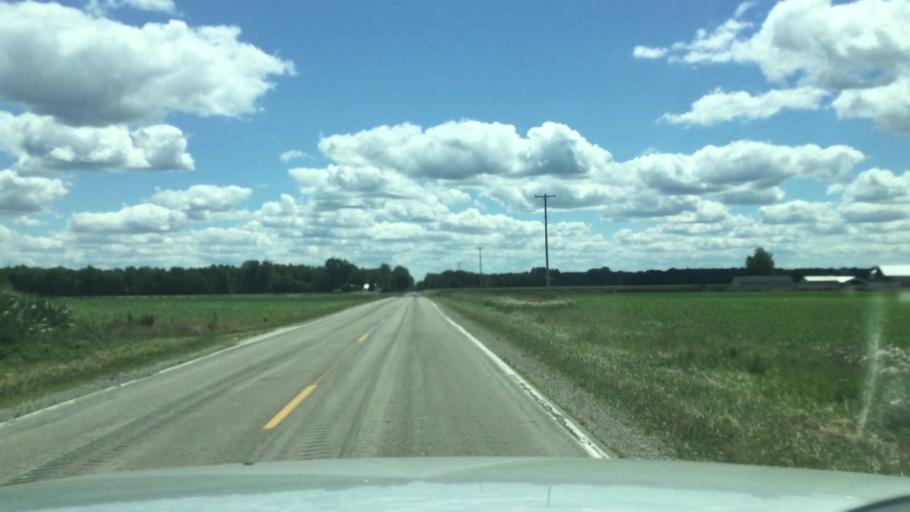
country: US
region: Michigan
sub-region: Saginaw County
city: Saint Charles
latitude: 43.3385
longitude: -84.1898
